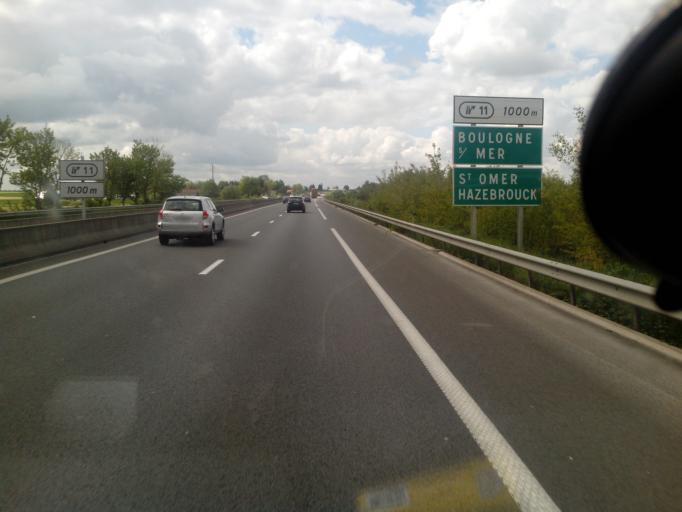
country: FR
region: Nord-Pas-de-Calais
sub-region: Departement du Nord
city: Meteren
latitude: 50.7286
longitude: 2.7135
